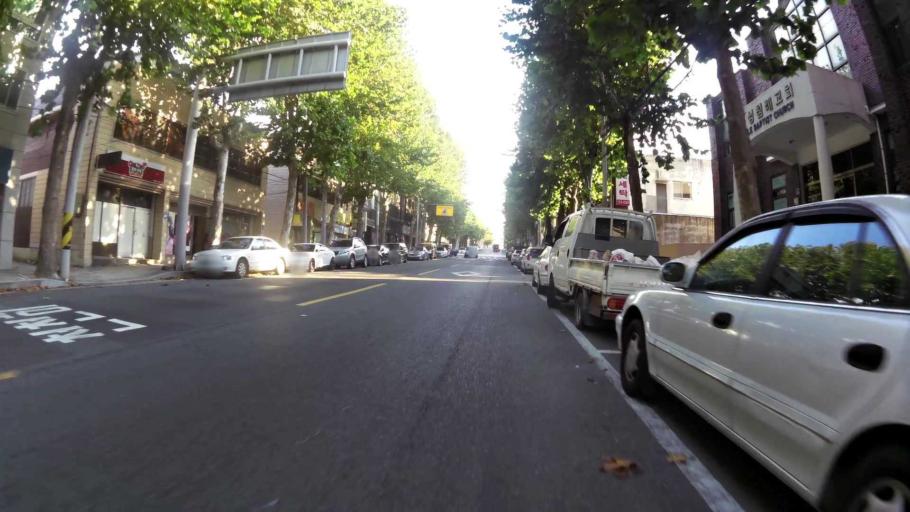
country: KR
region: Daegu
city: Daegu
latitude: 35.8643
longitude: 128.6392
